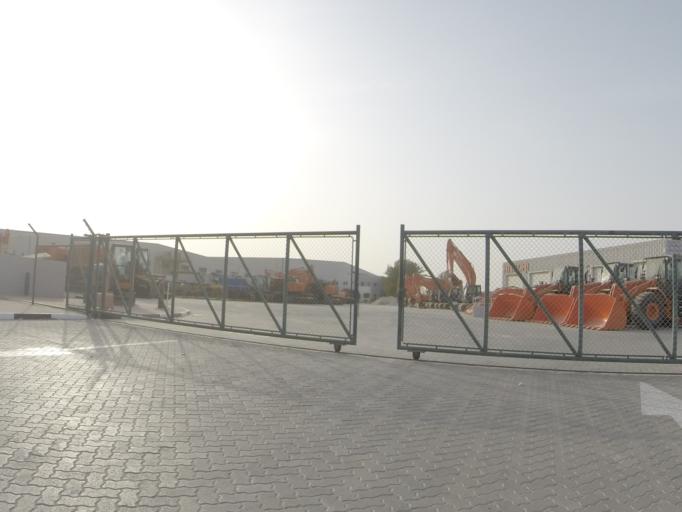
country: AE
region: Dubai
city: Dubai
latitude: 24.9513
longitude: 55.0635
